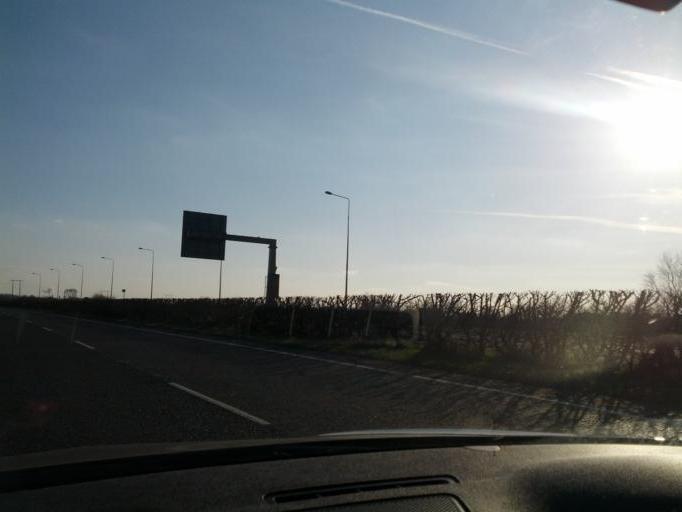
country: IE
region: Leinster
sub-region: Laois
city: Portlaoise
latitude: 53.0459
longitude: -7.2422
